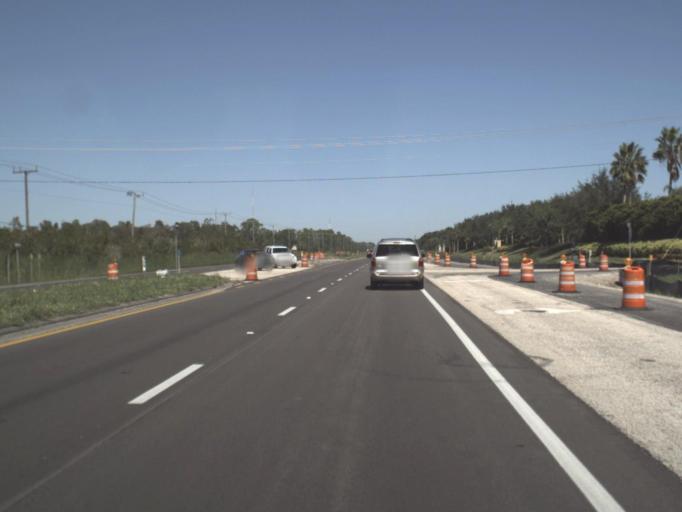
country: US
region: Florida
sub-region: Collier County
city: Lely Resort
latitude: 26.0320
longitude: -81.7005
